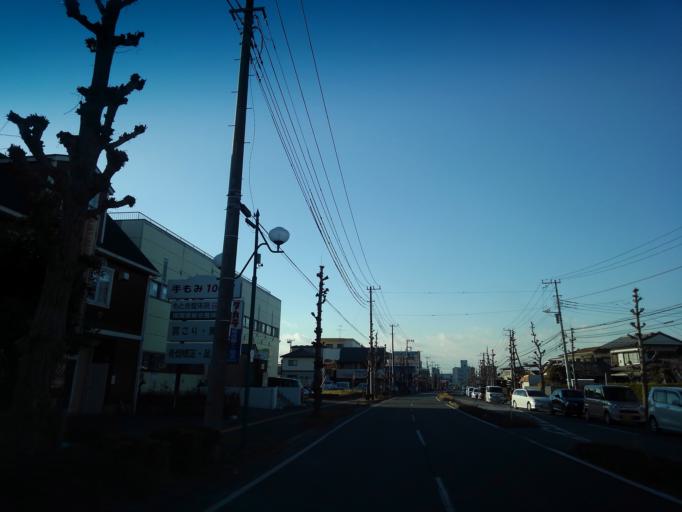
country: JP
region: Chiba
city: Kimitsu
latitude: 35.3325
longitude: 139.9027
